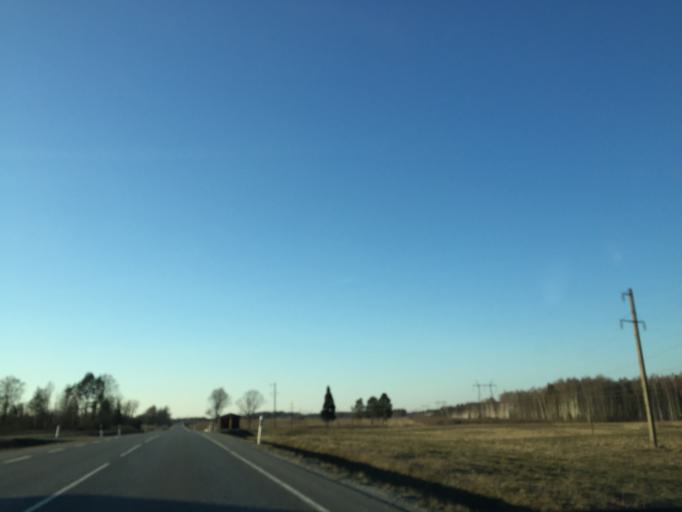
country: EE
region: Ida-Virumaa
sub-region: Johvi vald
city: Johvi
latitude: 59.2515
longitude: 27.5196
